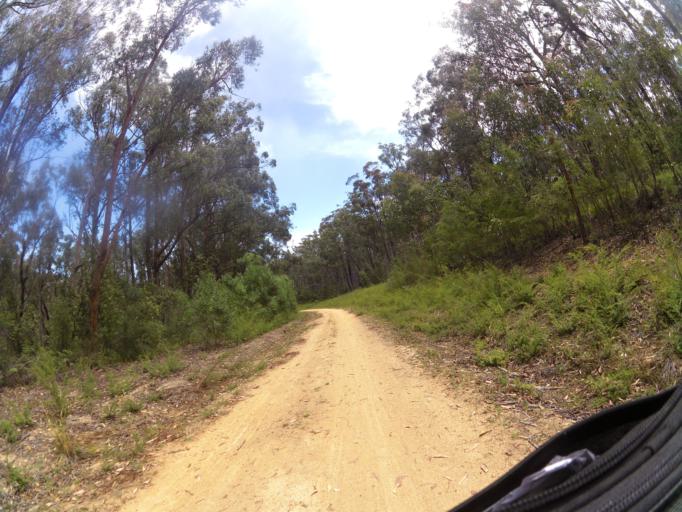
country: AU
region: Victoria
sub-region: East Gippsland
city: Lakes Entrance
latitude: -37.7401
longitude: 148.0063
